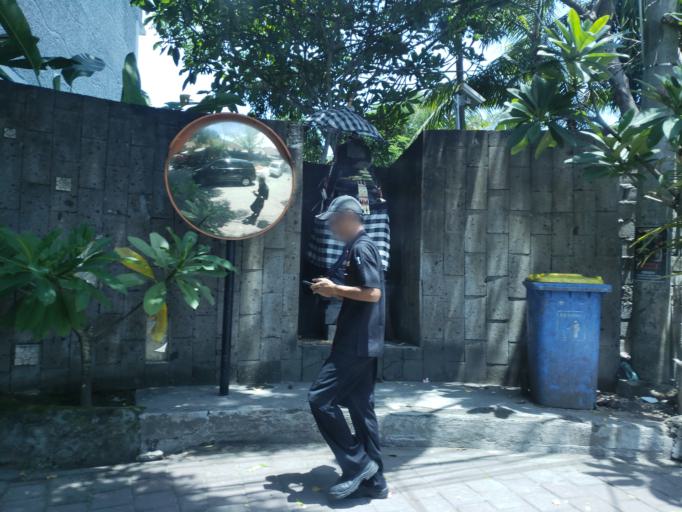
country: ID
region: Bali
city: Jimbaran
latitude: -8.7820
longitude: 115.1657
